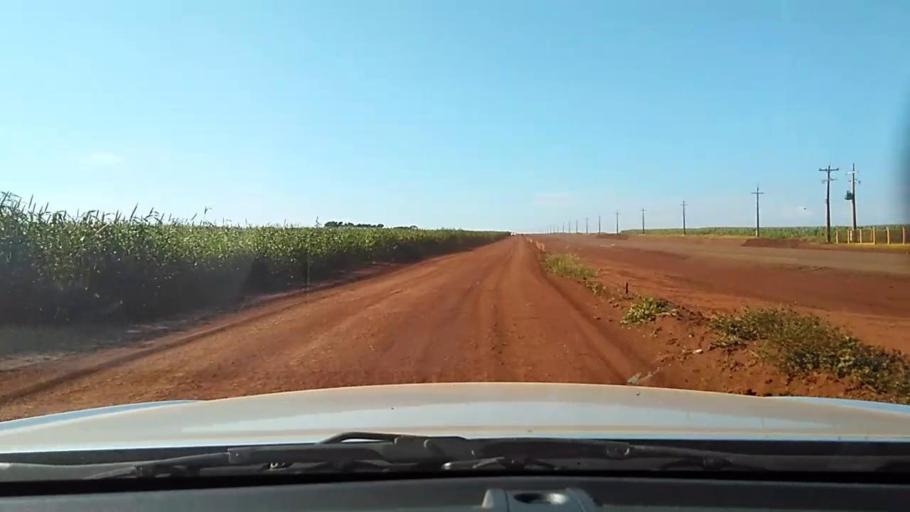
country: PY
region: Alto Parana
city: Naranjal
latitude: -25.9089
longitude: -55.4443
